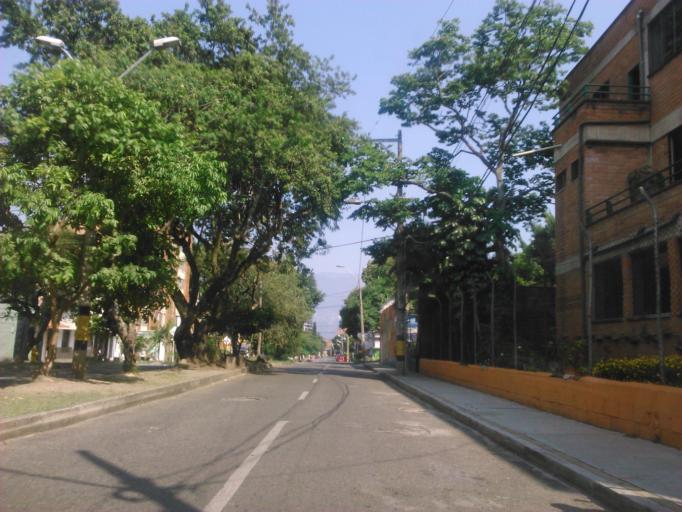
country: CO
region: Antioquia
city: Medellin
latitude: 6.2507
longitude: -75.6131
